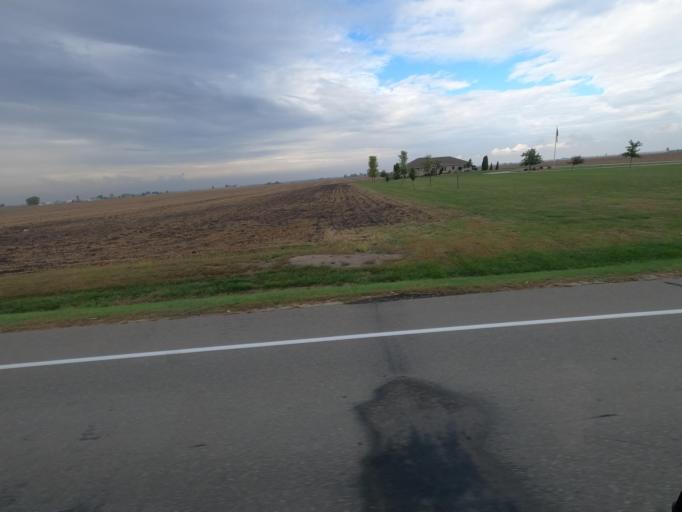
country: US
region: Iowa
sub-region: Henry County
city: Mount Pleasant
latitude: 40.7846
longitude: -91.6133
